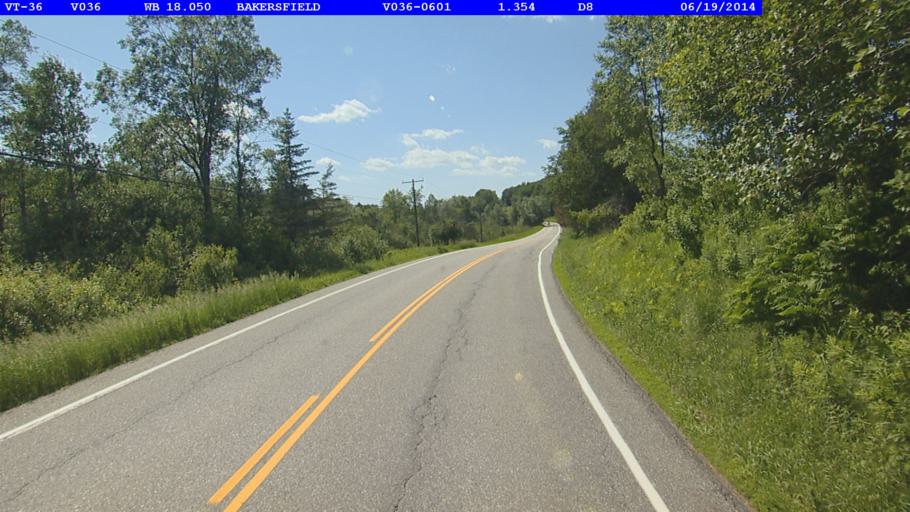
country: US
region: Vermont
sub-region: Franklin County
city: Enosburg Falls
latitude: 44.7818
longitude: -72.8239
